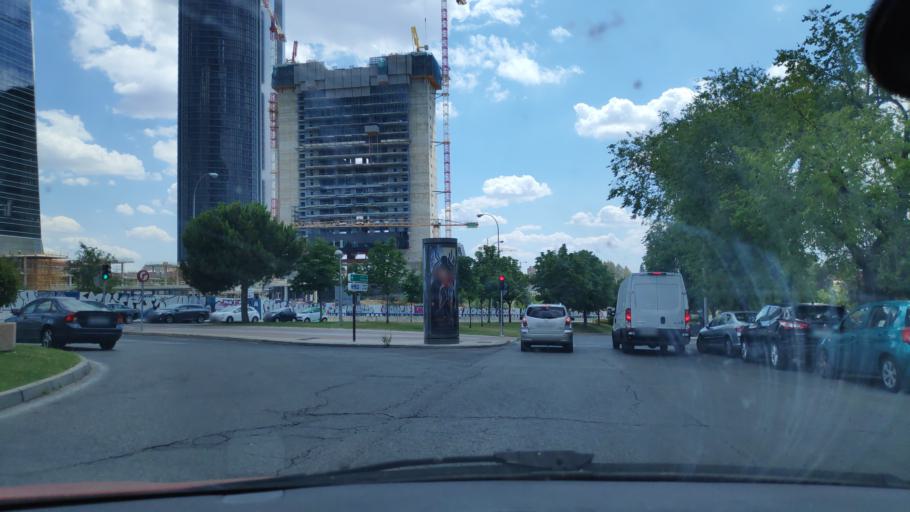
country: ES
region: Madrid
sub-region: Provincia de Madrid
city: Pinar de Chamartin
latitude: 40.4802
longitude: -3.6895
